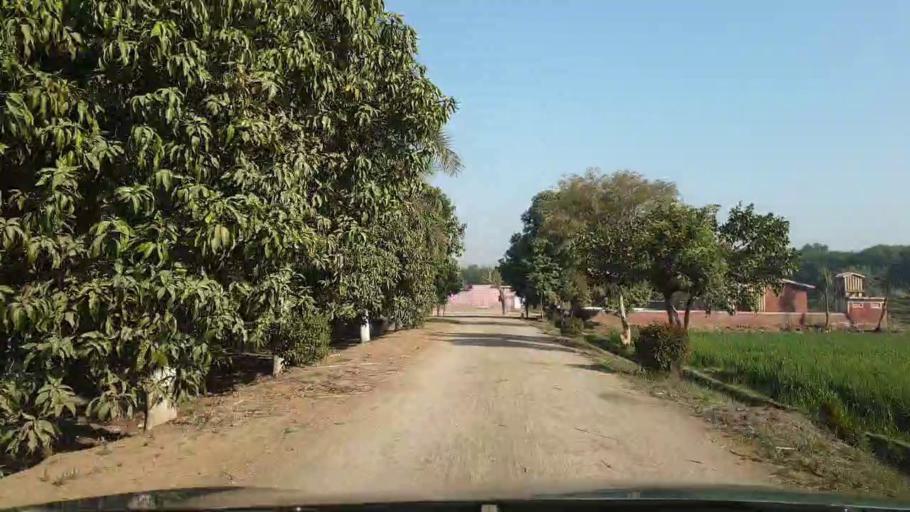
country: PK
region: Sindh
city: Tando Allahyar
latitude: 25.4953
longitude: 68.7090
